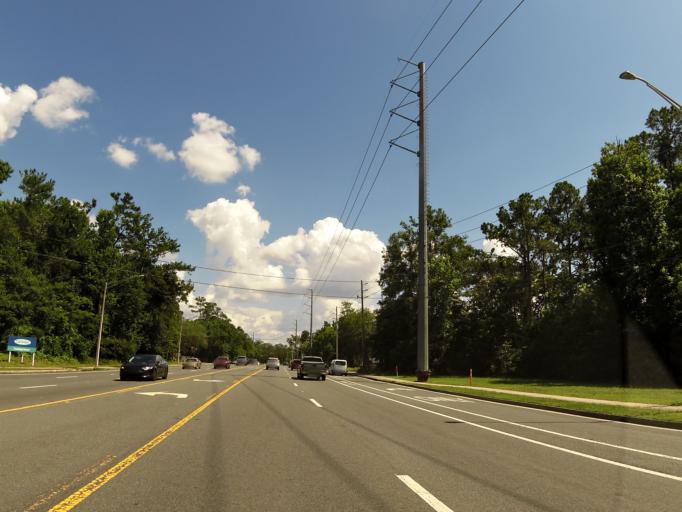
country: US
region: Florida
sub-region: Saint Johns County
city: Fruit Cove
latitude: 30.1638
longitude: -81.6008
